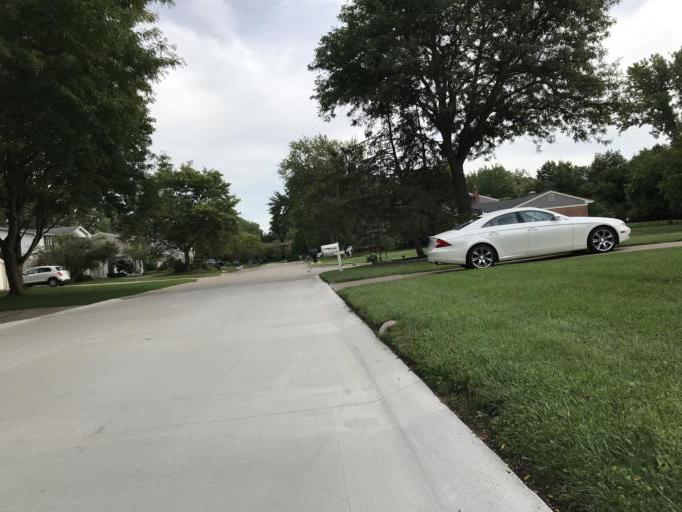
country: US
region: Michigan
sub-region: Oakland County
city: Franklin
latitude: 42.4824
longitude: -83.3224
